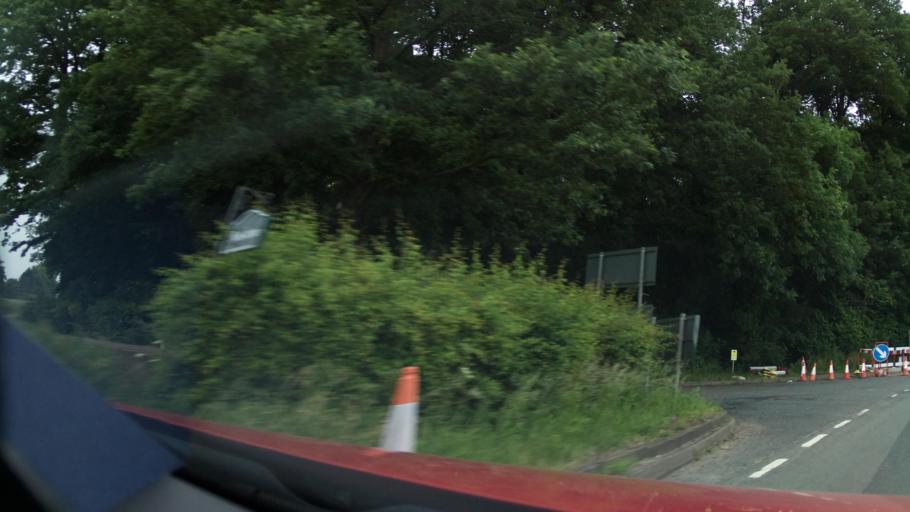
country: GB
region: England
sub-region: Derbyshire
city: Netherseal
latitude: 52.6980
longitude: -1.5549
